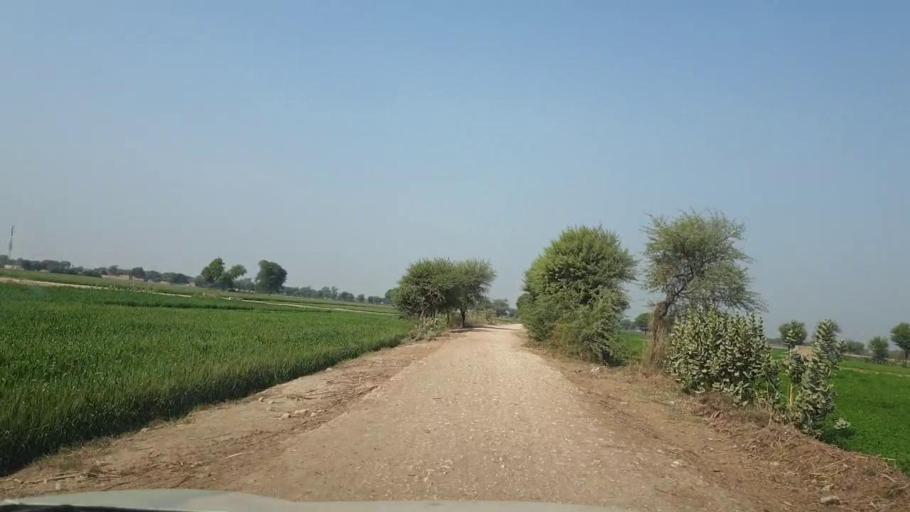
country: PK
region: Sindh
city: Bhit Shah
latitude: 25.7470
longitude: 68.4593
